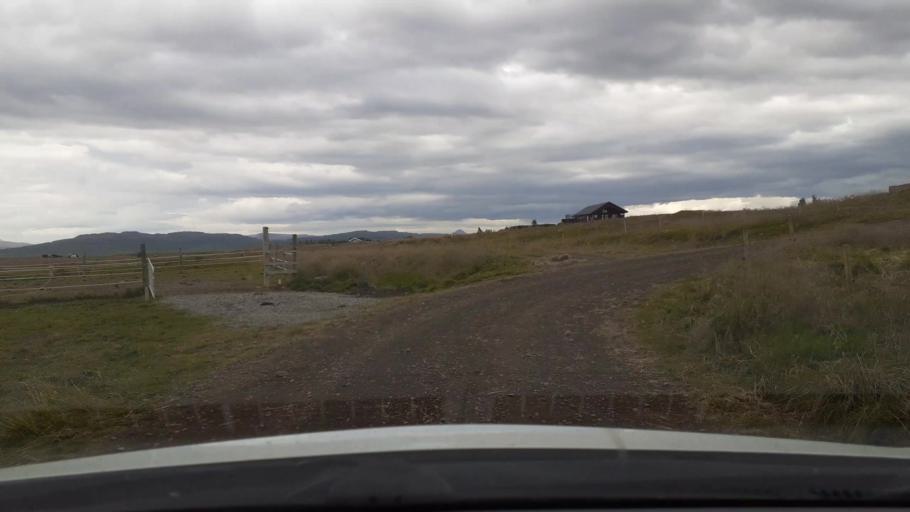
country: IS
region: West
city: Borgarnes
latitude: 64.6539
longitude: -21.8787
